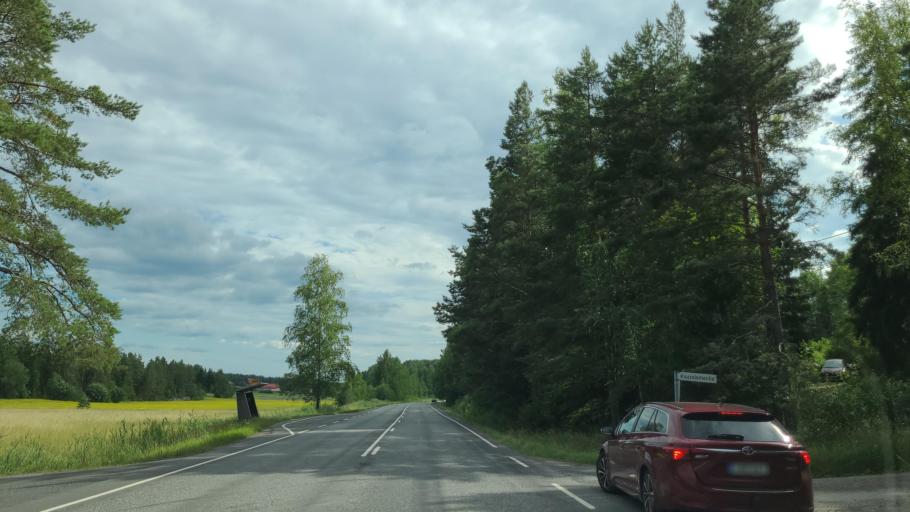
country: FI
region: Varsinais-Suomi
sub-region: Turku
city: Merimasku
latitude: 60.4444
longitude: 21.8971
